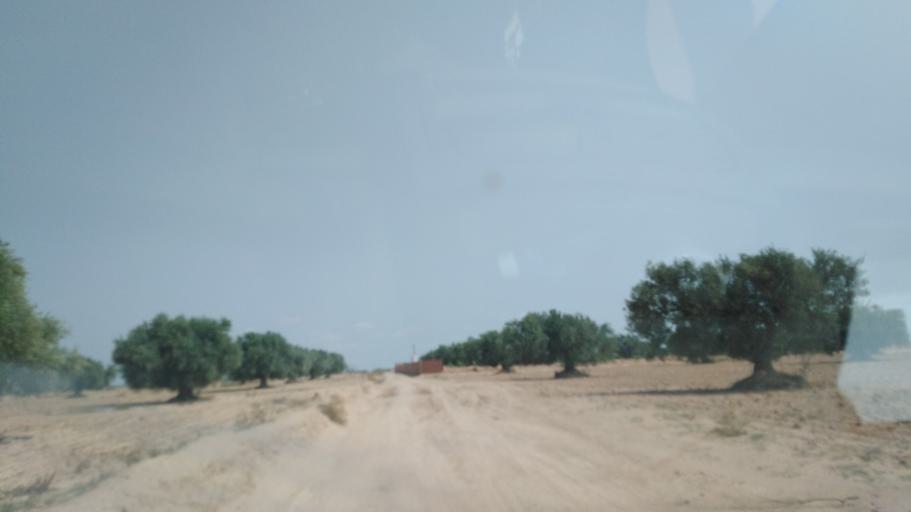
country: TN
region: Safaqis
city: Sfax
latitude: 34.6586
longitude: 10.5602
